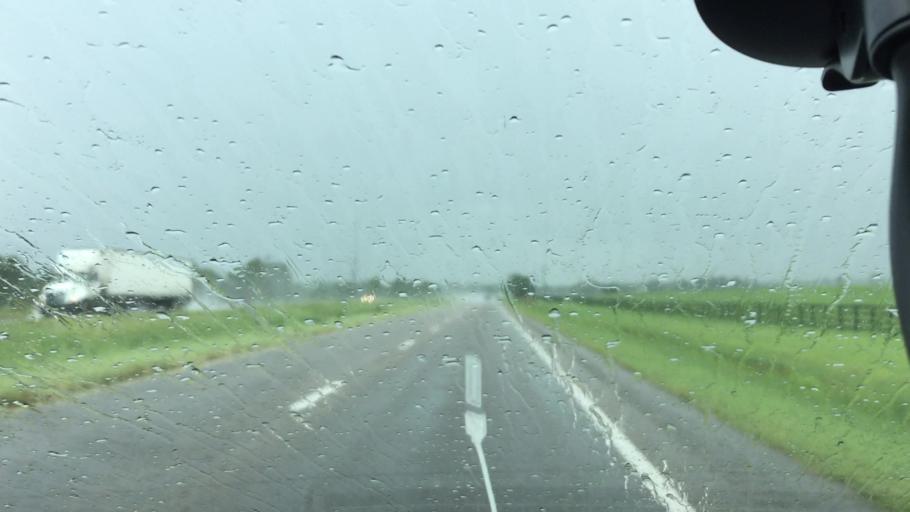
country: US
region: Alabama
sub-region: Montgomery County
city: Pike Road
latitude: 32.2354
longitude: -86.1263
